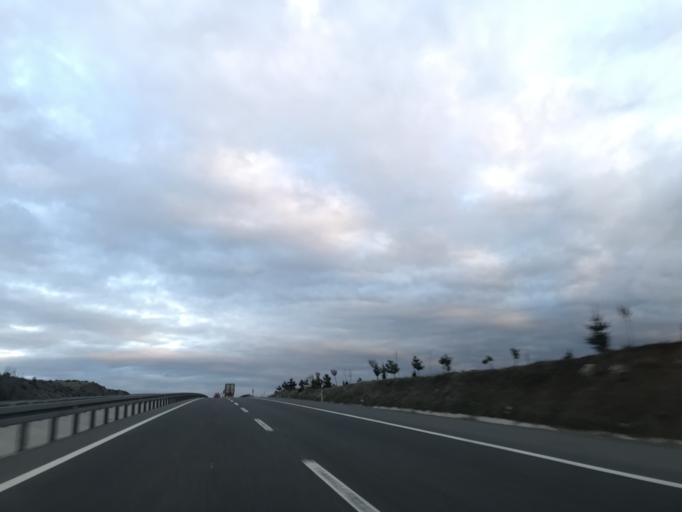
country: TR
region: Ankara
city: Ikizce
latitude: 39.5144
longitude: 32.8692
